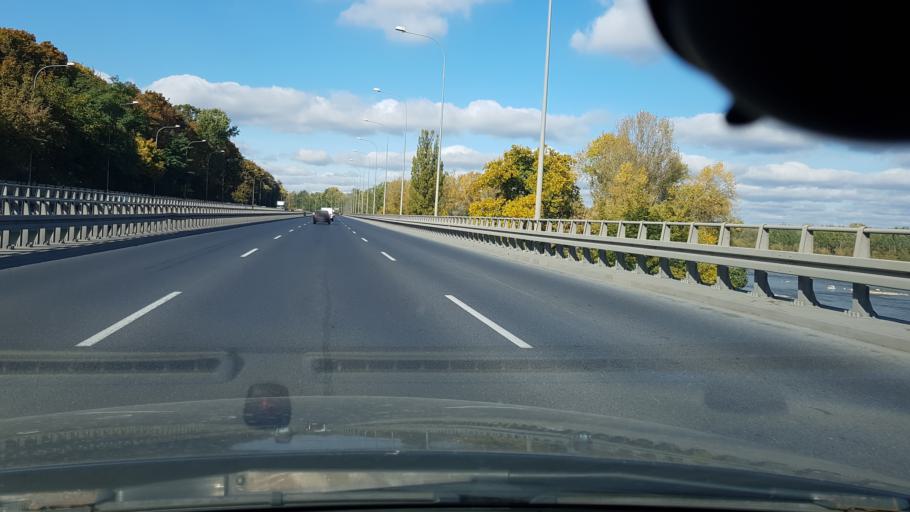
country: PL
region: Masovian Voivodeship
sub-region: Warszawa
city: Bialoleka
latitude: 52.2966
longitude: 20.9633
